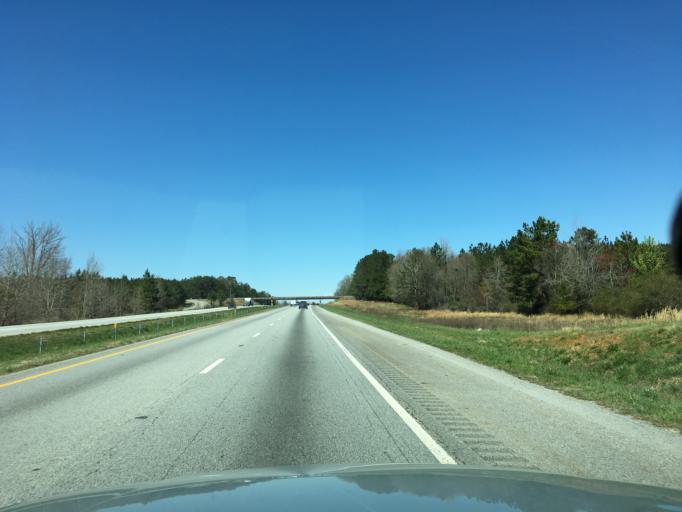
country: US
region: South Carolina
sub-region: Spartanburg County
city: Inman
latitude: 35.0568
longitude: -82.0490
